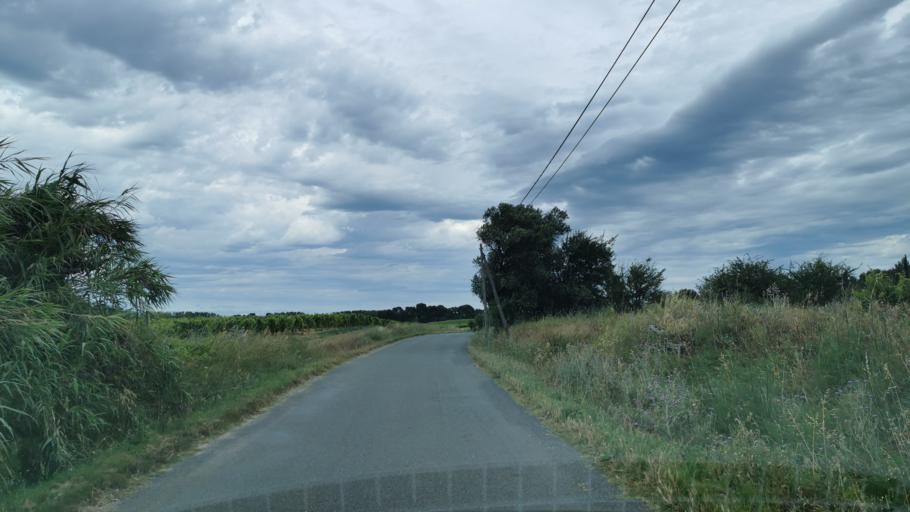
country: FR
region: Languedoc-Roussillon
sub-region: Departement de l'Aude
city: Moussan
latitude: 43.2384
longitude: 2.9615
